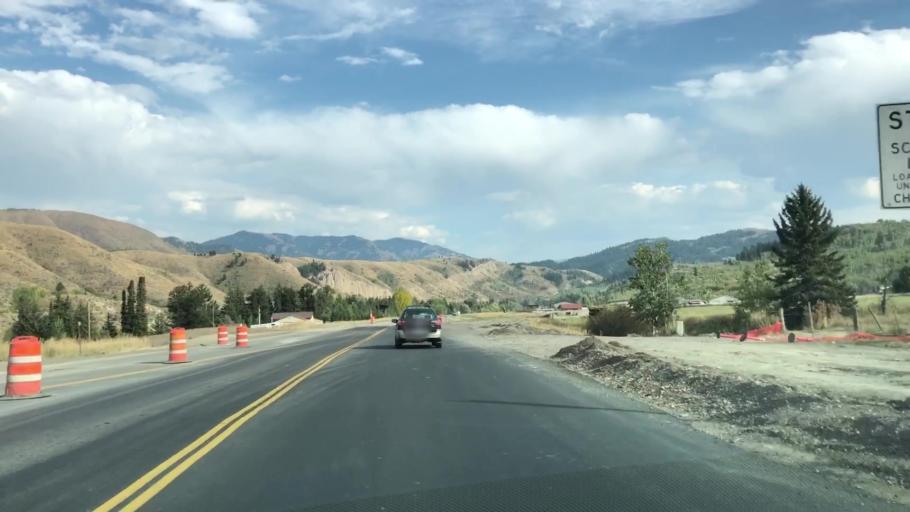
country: US
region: Wyoming
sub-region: Teton County
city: South Park
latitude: 43.3709
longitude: -110.7400
